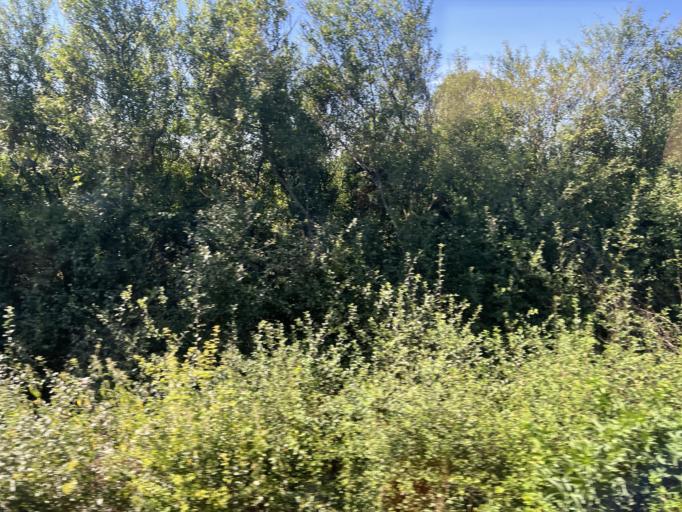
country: GB
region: England
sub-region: Lincolnshire
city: Heckington
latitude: 52.9673
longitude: -0.2394
